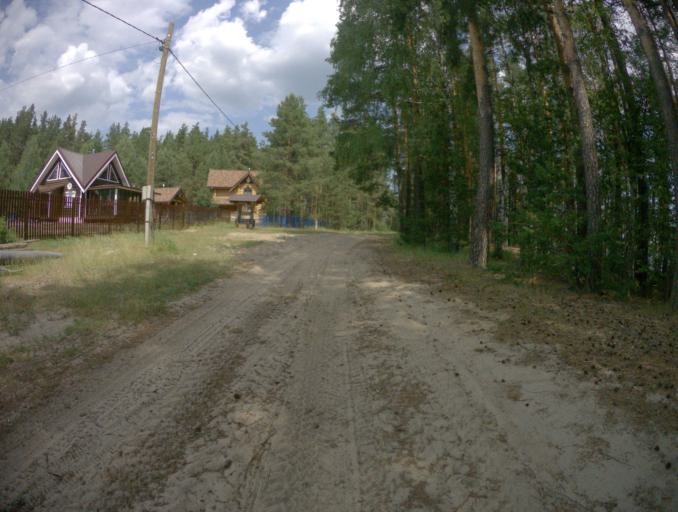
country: RU
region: Ivanovo
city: Talitsy
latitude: 56.3953
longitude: 42.3820
